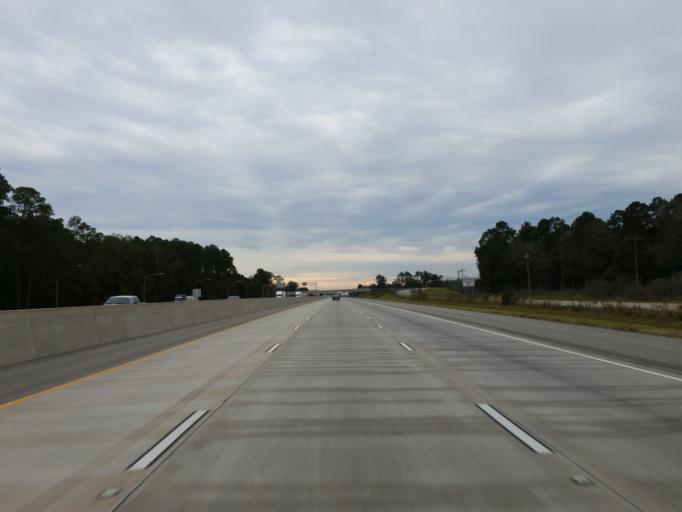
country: US
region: Georgia
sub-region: Cook County
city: Sparks
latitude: 31.2436
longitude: -83.4664
